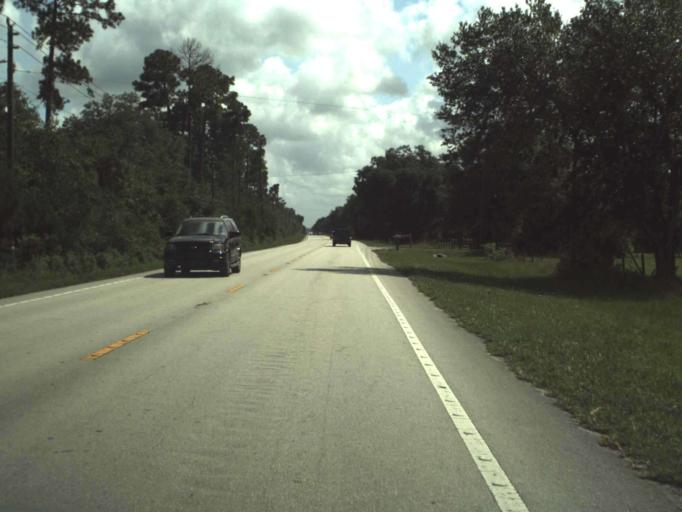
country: US
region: Florida
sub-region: Volusia County
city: Lake Helen
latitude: 28.9230
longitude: -81.1165
